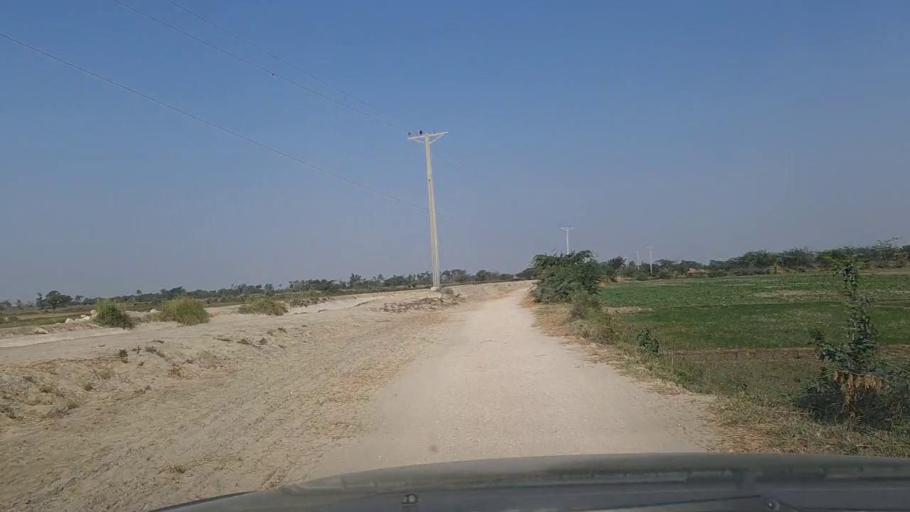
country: PK
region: Sindh
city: Mirpur Sakro
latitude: 24.5127
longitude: 67.8044
